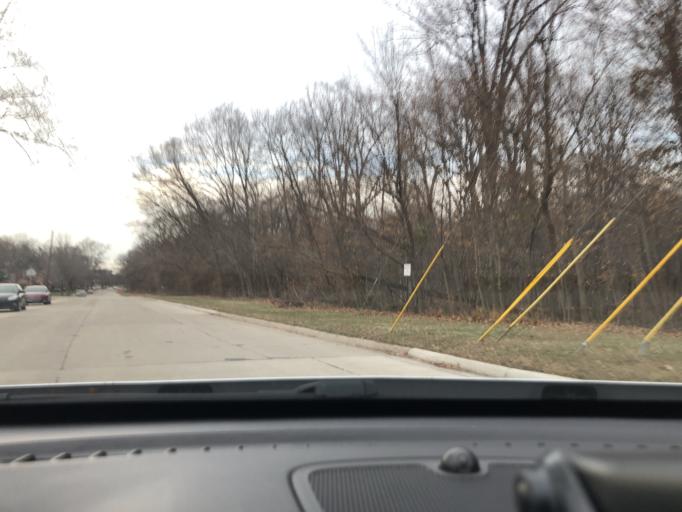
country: US
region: Michigan
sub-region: Wayne County
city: Allen Park
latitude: 42.2903
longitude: -83.2236
